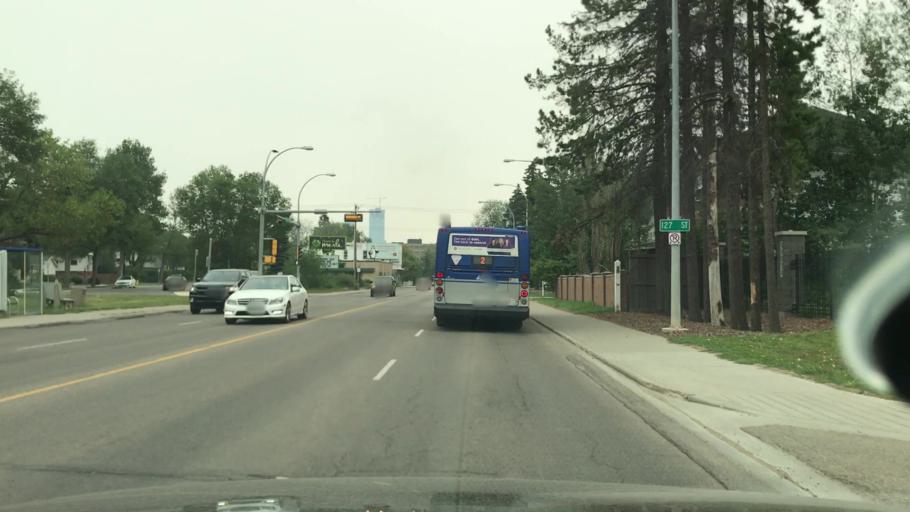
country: CA
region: Alberta
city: Edmonton
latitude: 53.5477
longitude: -113.5422
